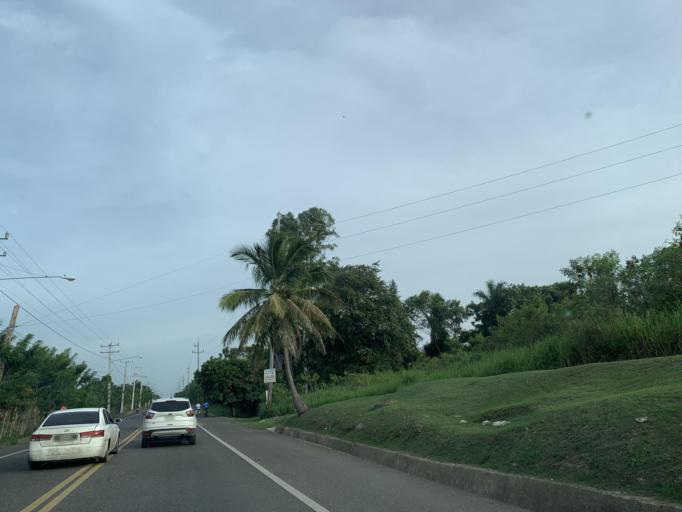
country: DO
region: Puerto Plata
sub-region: Puerto Plata
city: Puerto Plata
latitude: 19.7335
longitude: -70.6284
